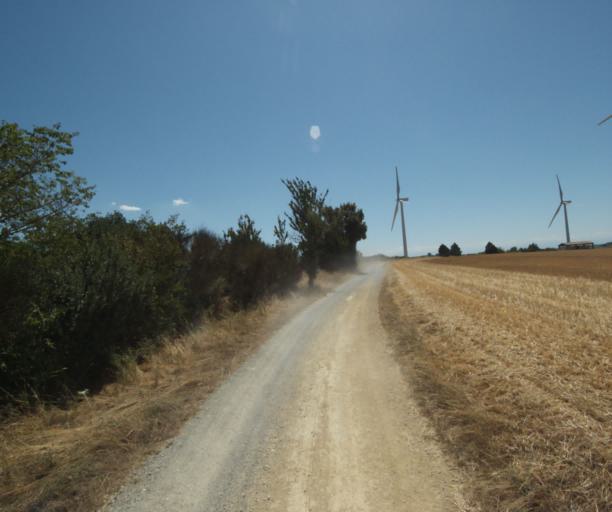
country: FR
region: Midi-Pyrenees
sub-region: Departement de la Haute-Garonne
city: Saint-Felix-Lauragais
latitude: 43.4653
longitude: 1.9210
